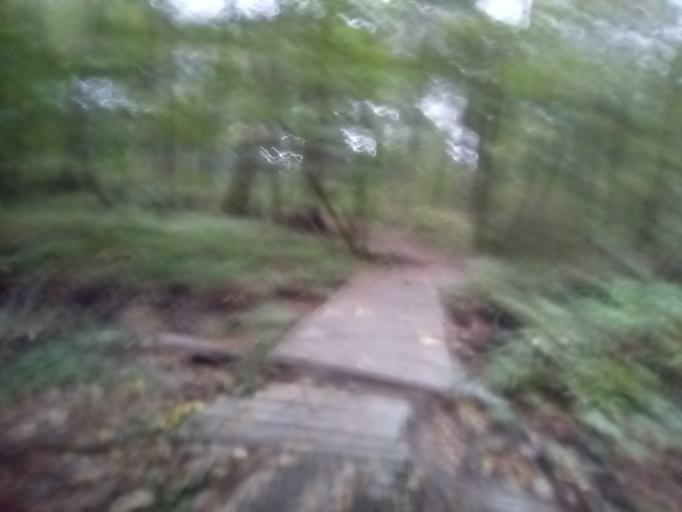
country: RU
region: Moskovskaya
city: Kokoshkino
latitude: 55.6192
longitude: 37.1664
